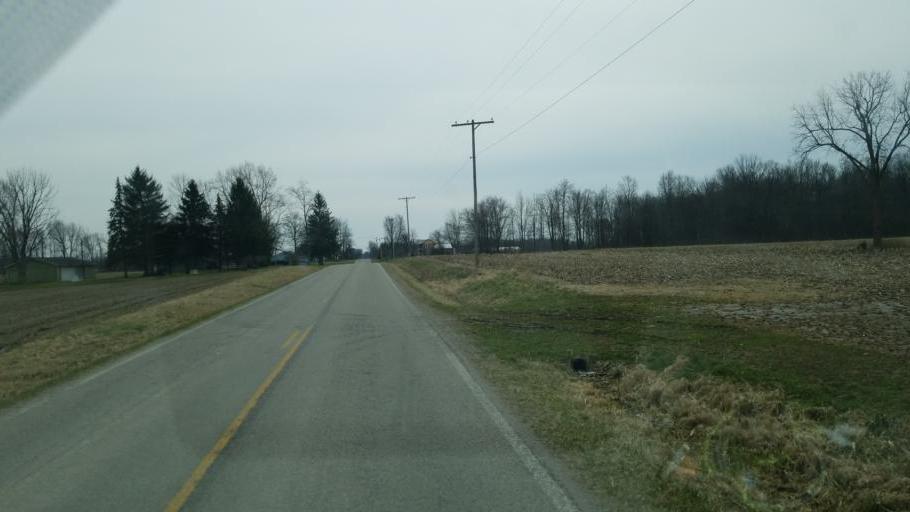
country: US
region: Ohio
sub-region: Huron County
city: Wakeman
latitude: 41.1709
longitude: -82.4902
